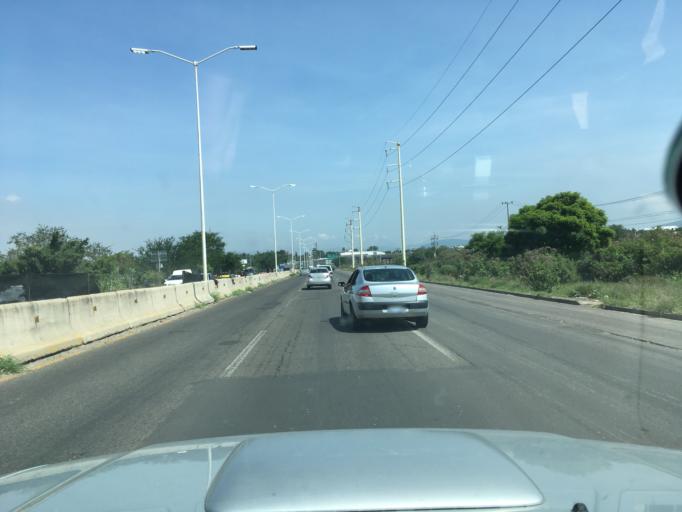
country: MX
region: Jalisco
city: Tonala
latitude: 20.6803
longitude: -103.2424
